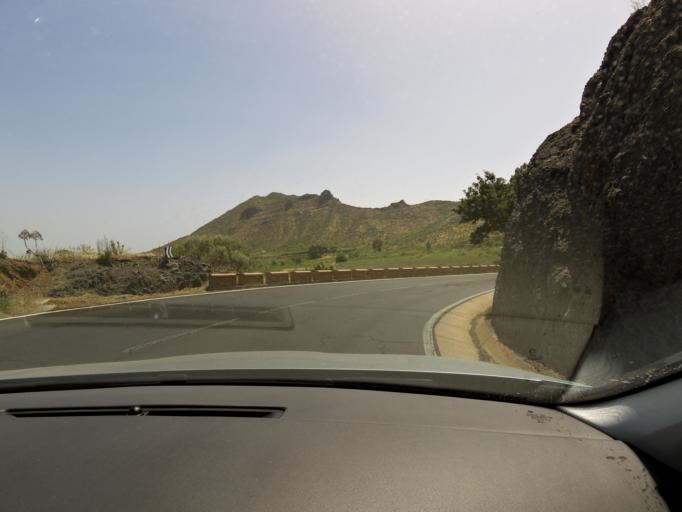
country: ES
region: Canary Islands
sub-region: Provincia de Santa Cruz de Tenerife
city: Santiago del Teide
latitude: 28.3041
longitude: -16.8128
